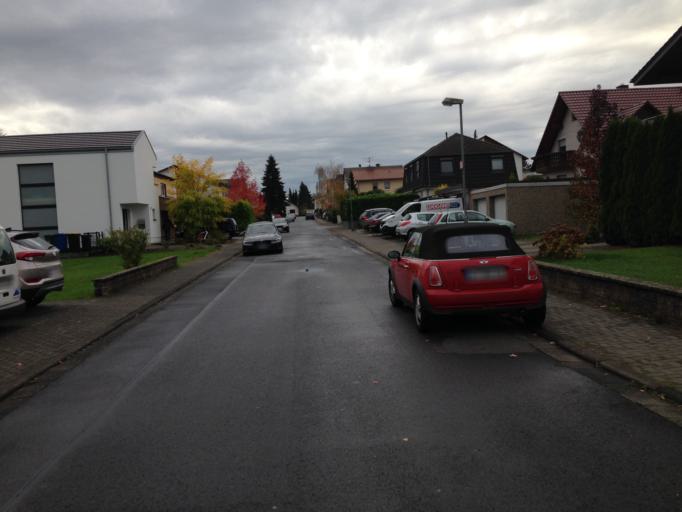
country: DE
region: Hesse
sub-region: Regierungsbezirk Giessen
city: Heuchelheim
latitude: 50.5872
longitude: 8.6286
